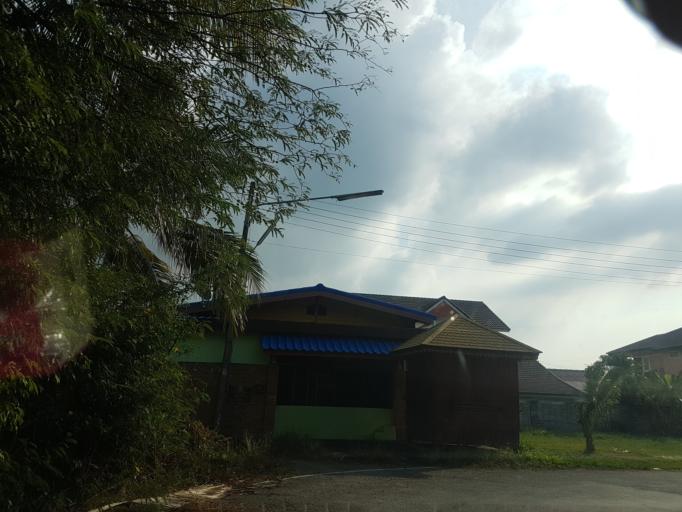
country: TH
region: Lop Buri
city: Lop Buri
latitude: 14.7701
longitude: 100.6966
